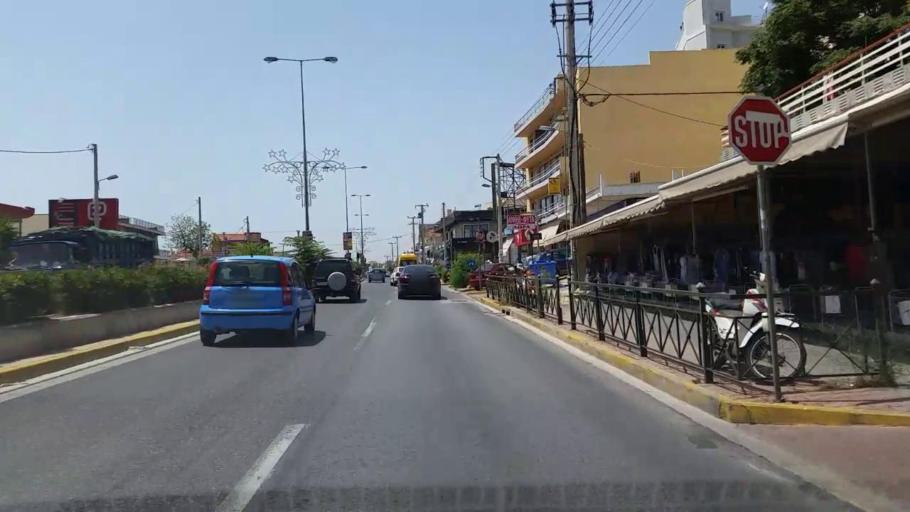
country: GR
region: Attica
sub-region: Nomarchia Anatolikis Attikis
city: Gerakas
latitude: 38.0080
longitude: 23.8570
